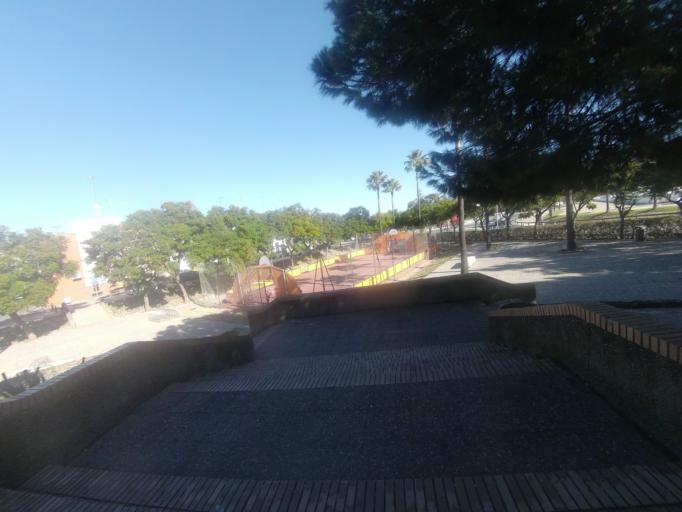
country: ES
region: Andalusia
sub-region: Provincia de Huelva
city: Palos de la Frontera
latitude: 37.2271
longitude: -6.8899
